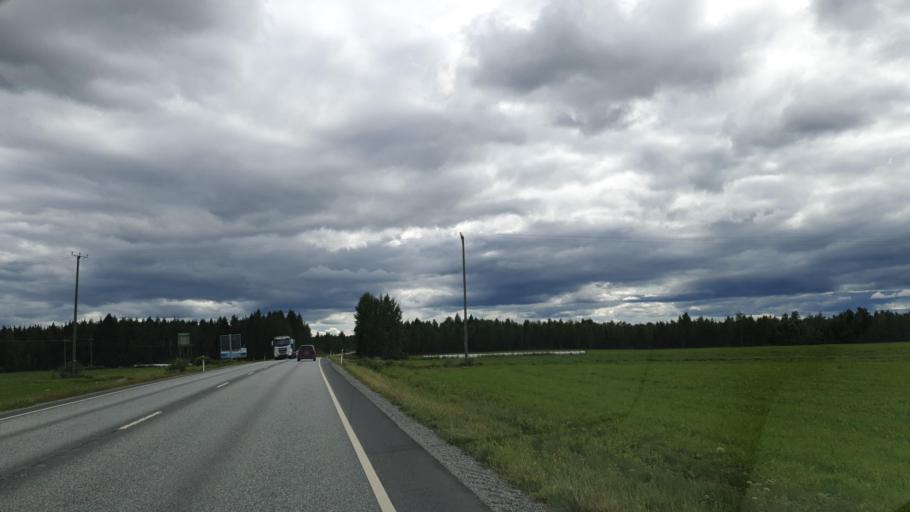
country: FI
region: Northern Savo
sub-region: Ylae-Savo
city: Sonkajaervi
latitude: 63.8651
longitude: 27.4412
